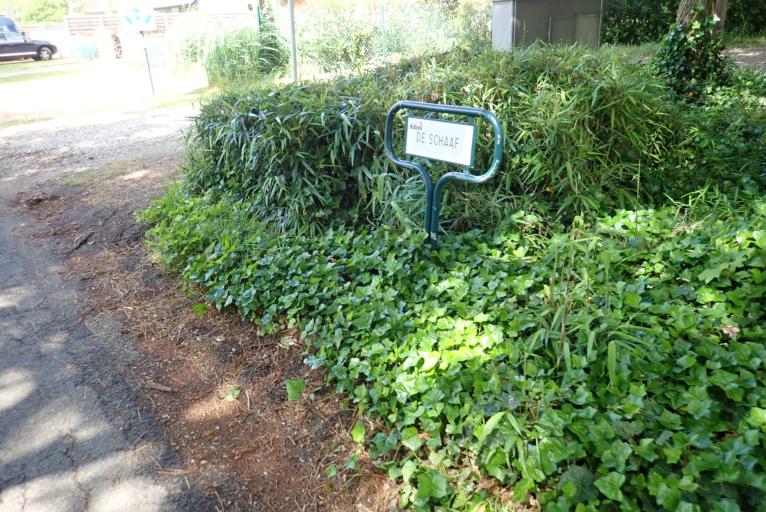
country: BE
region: Flanders
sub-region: Provincie Antwerpen
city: Zoersel
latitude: 51.2835
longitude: 4.7192
